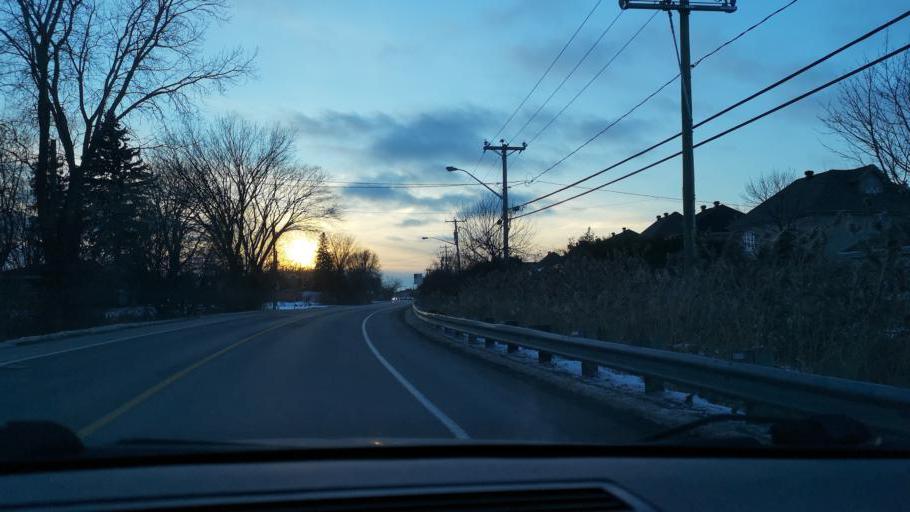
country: CA
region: Quebec
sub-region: Laval
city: Laval
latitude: 45.5760
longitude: -73.7598
